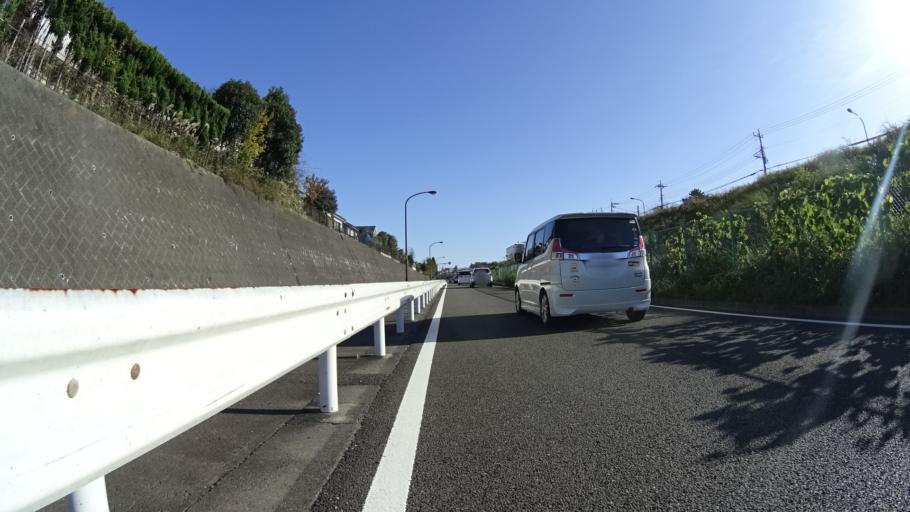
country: JP
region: Tokyo
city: Hino
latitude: 35.6112
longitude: 139.4192
